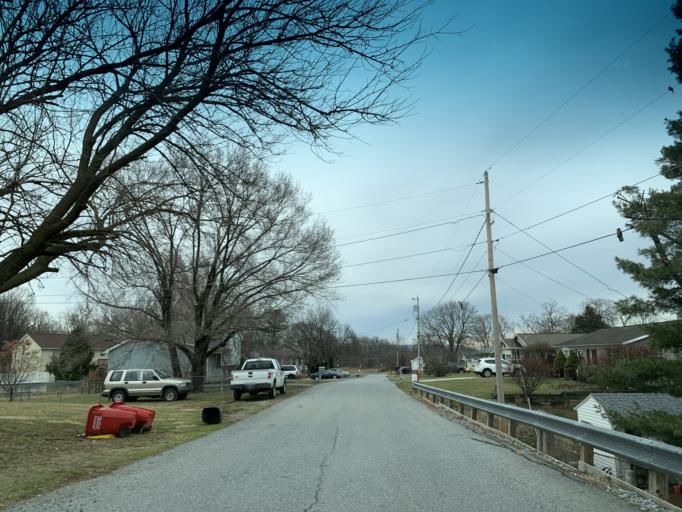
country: US
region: West Virginia
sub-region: Jefferson County
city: Ranson
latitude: 39.3055
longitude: -77.8583
